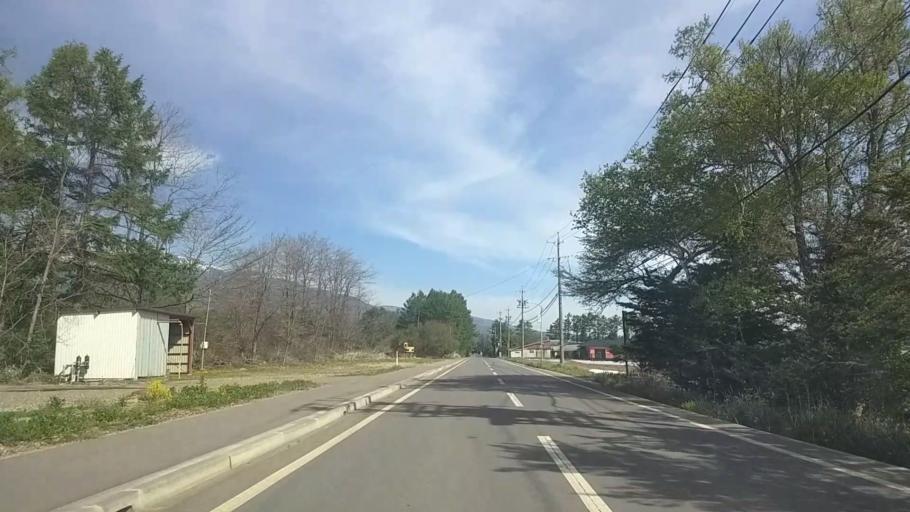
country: JP
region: Yamanashi
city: Nirasaki
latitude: 35.9488
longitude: 138.4756
